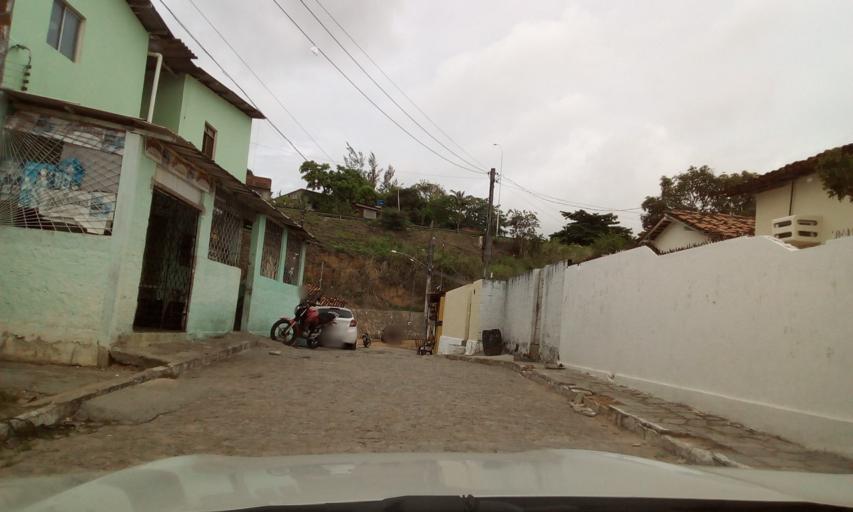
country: BR
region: Paraiba
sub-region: Joao Pessoa
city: Joao Pessoa
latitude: -7.1353
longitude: -34.8554
